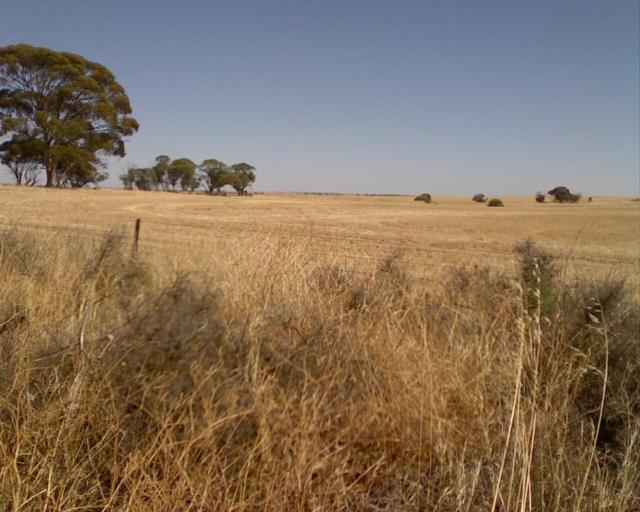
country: AU
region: Western Australia
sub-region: Wongan-Ballidu
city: Wongan Hills
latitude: -30.3844
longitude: 116.7850
